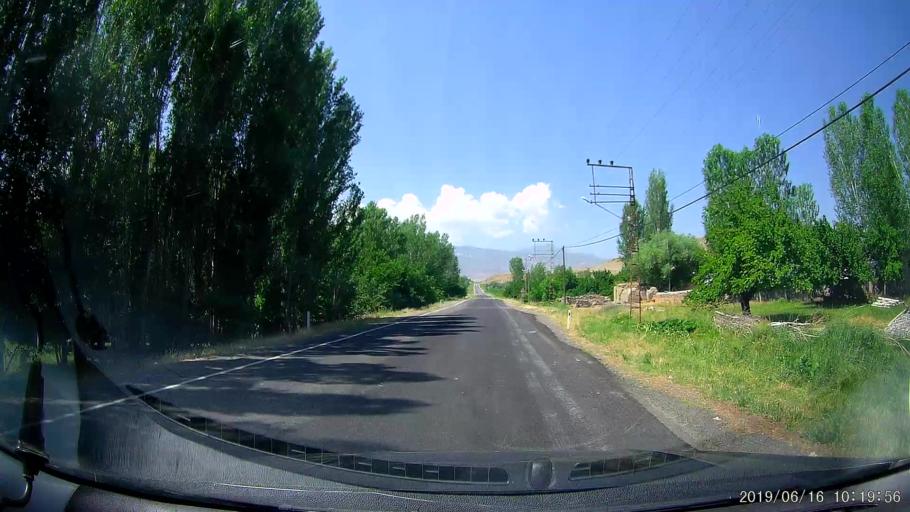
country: TR
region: Igdir
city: Tuzluca
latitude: 40.1519
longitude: 43.6524
